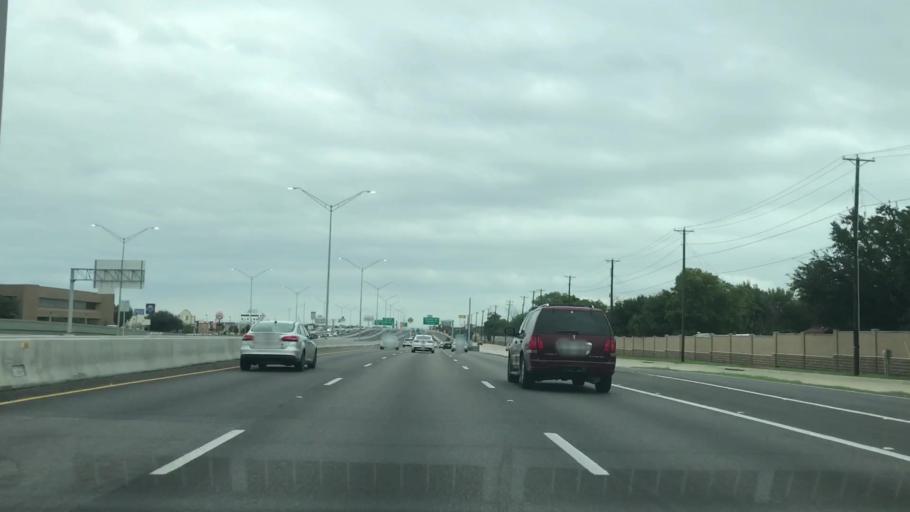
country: US
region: Texas
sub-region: Dallas County
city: Irving
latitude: 32.8370
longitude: -96.9847
